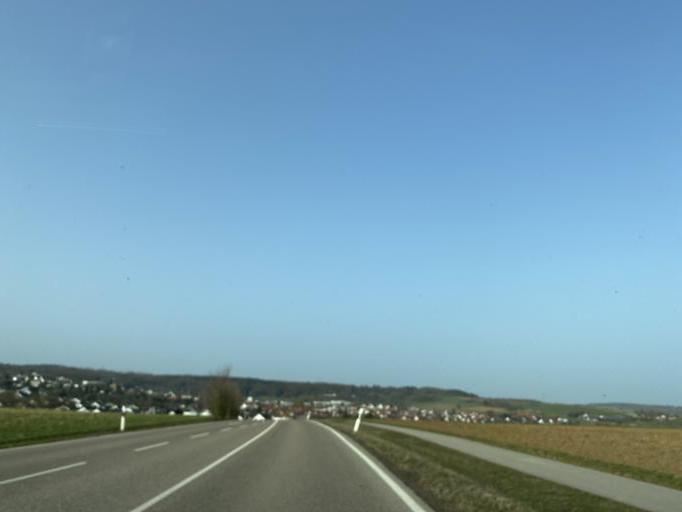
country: DE
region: Baden-Wuerttemberg
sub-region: Karlsruhe Region
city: Wiernsheim
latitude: 48.8910
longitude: 8.8648
